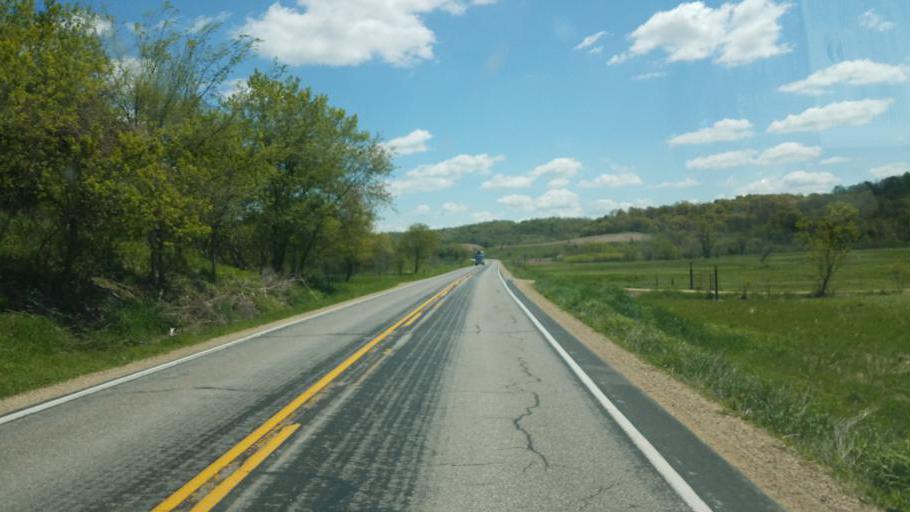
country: US
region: Wisconsin
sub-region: Vernon County
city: Hillsboro
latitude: 43.6450
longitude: -90.4191
